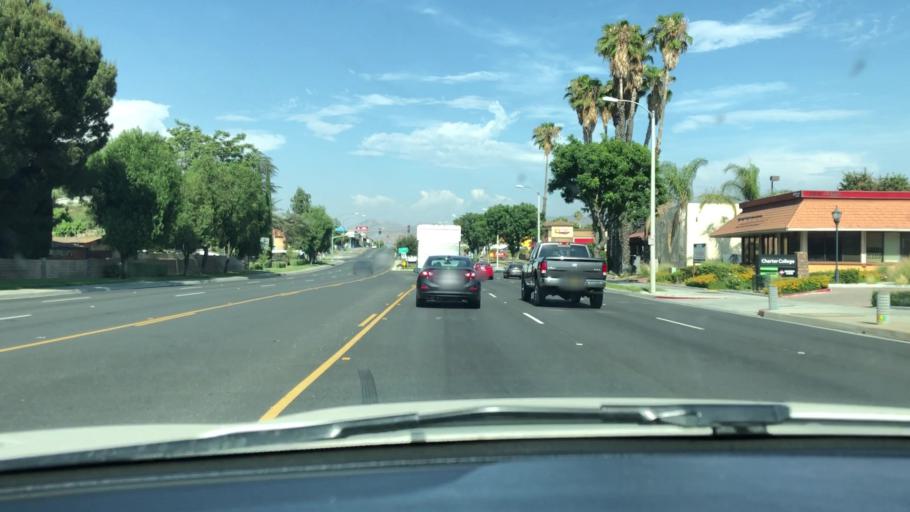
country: US
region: California
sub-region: Los Angeles County
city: Santa Clarita
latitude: 34.4156
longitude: -118.4685
